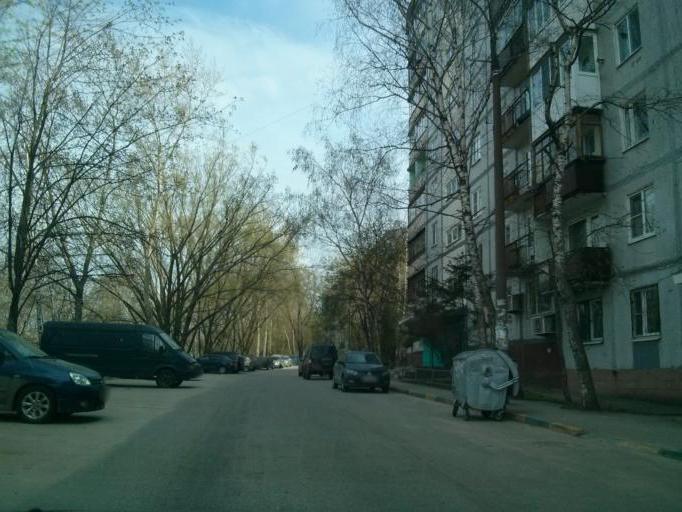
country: RU
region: Nizjnij Novgorod
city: Afonino
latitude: 56.2994
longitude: 44.0627
